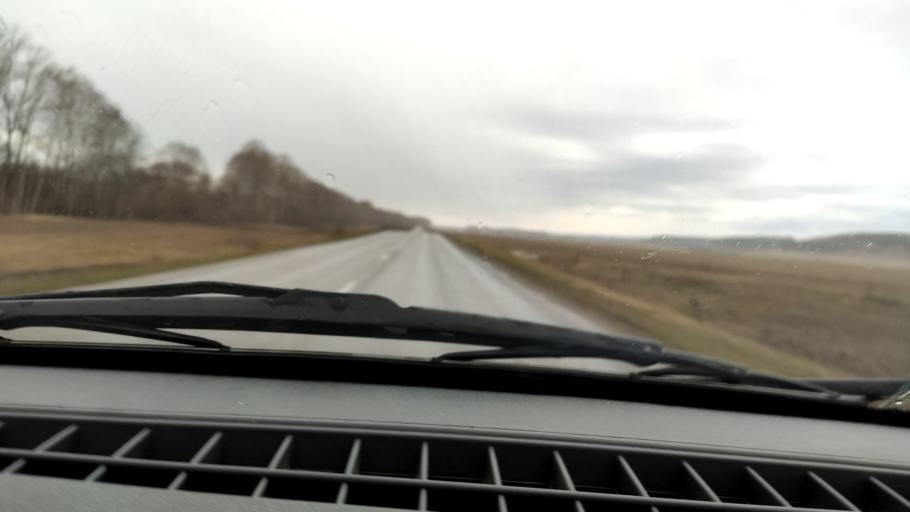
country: RU
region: Bashkortostan
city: Chekmagush
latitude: 55.1249
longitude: 54.7129
